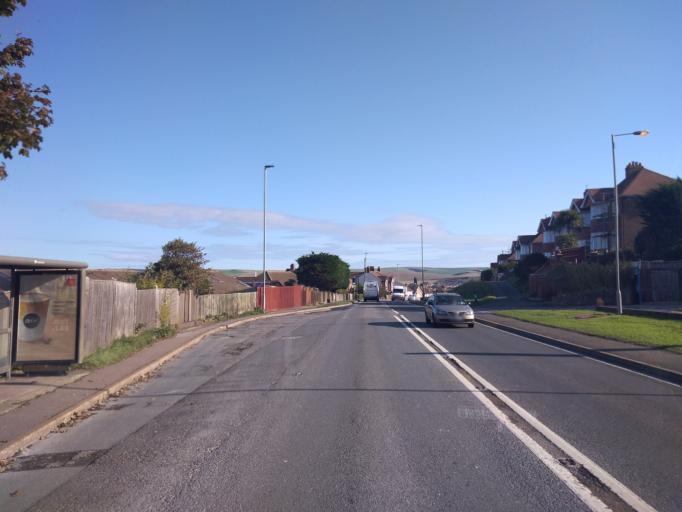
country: GB
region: England
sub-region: East Sussex
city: Newhaven
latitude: 50.7926
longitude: 0.0404
